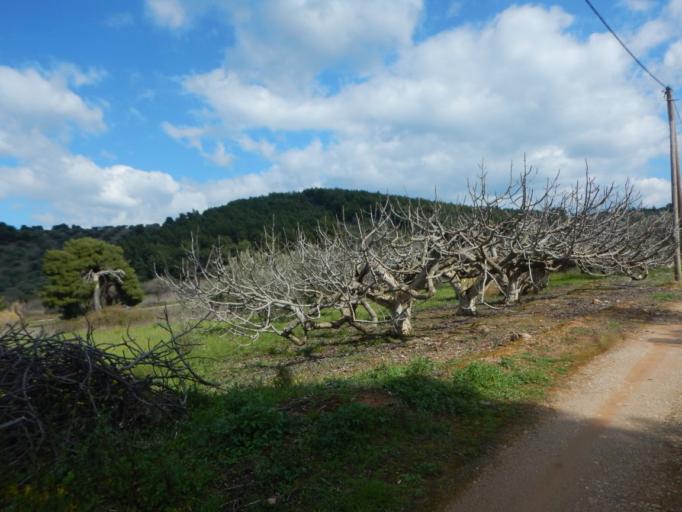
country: GR
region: Attica
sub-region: Nomarchia Anatolikis Attikis
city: Markopoulo Oropou
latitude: 38.2974
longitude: 23.8384
